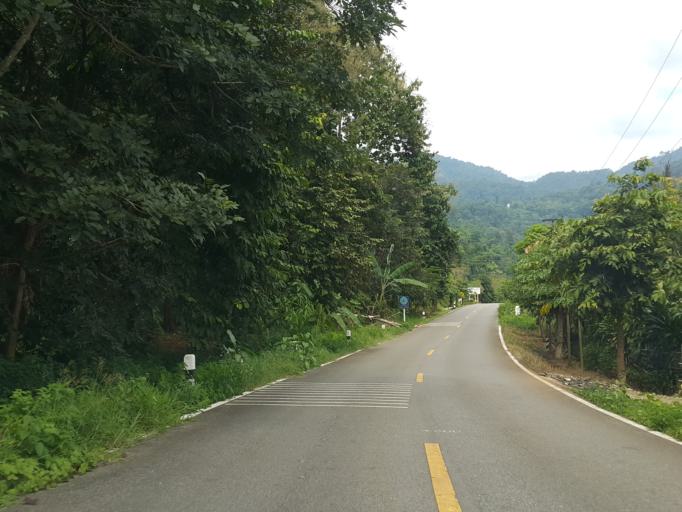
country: TH
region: Mae Hong Son
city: Mae Hong Son
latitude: 19.4779
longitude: 97.9647
